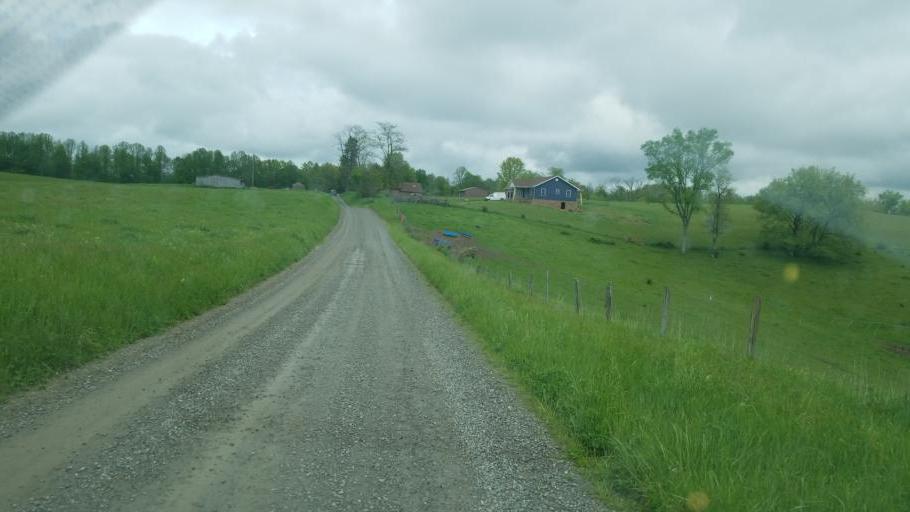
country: US
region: Ohio
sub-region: Harrison County
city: Cadiz
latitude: 40.3696
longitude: -81.1489
